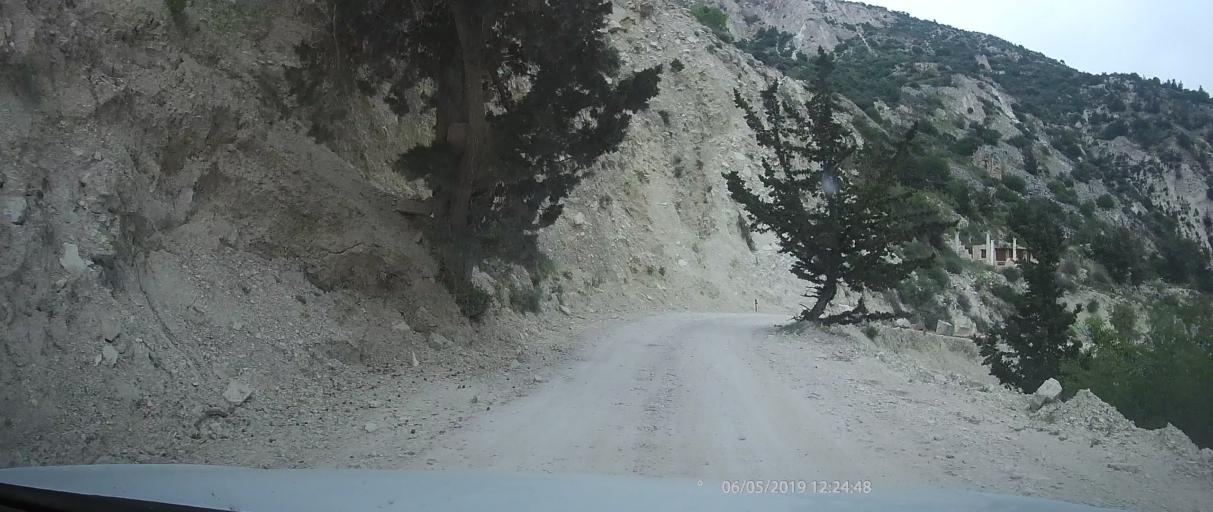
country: CY
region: Pafos
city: Tala
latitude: 34.8697
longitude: 32.4337
